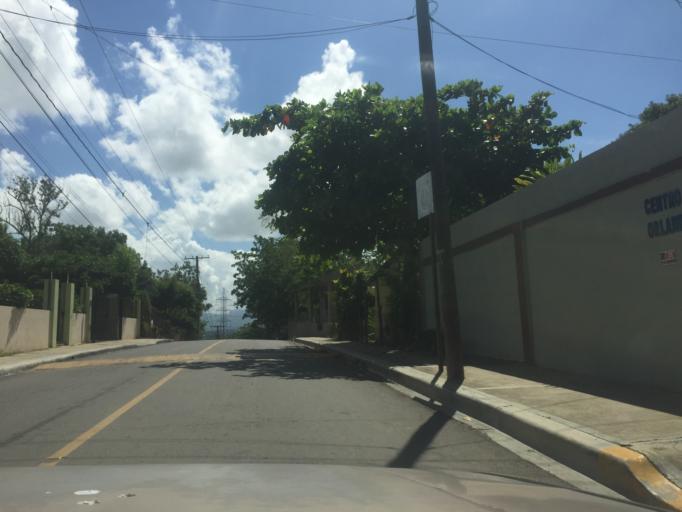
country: DO
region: Santiago
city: Santiago de los Caballeros
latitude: 19.4473
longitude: -70.7556
